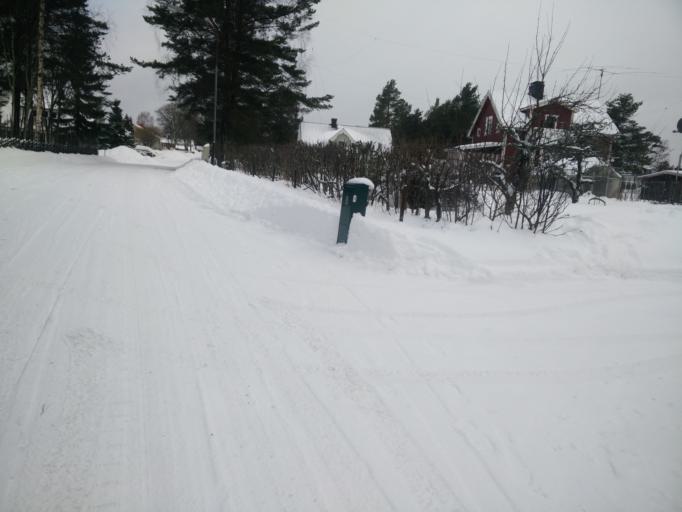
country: SE
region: Vaesternorrland
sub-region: Sundsvalls Kommun
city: Nolby
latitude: 62.2898
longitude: 17.3692
